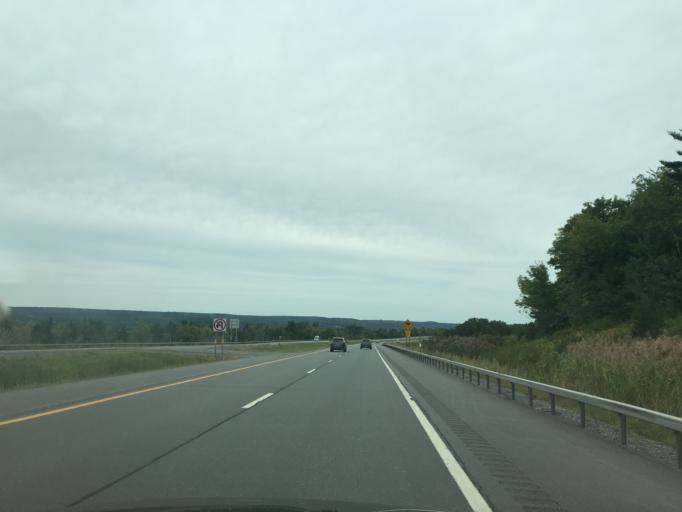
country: US
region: New York
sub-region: Albany County
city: Altamont
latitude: 42.7471
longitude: -74.1593
